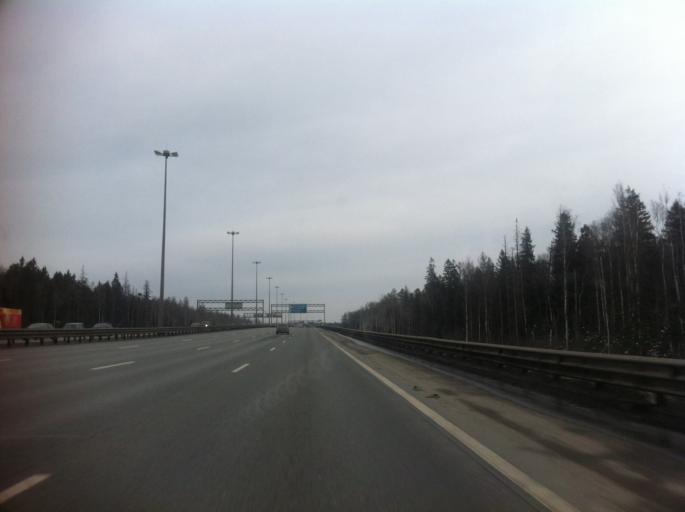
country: RU
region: St.-Petersburg
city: Krasnogvargeisky
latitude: 59.9147
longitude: 30.5260
